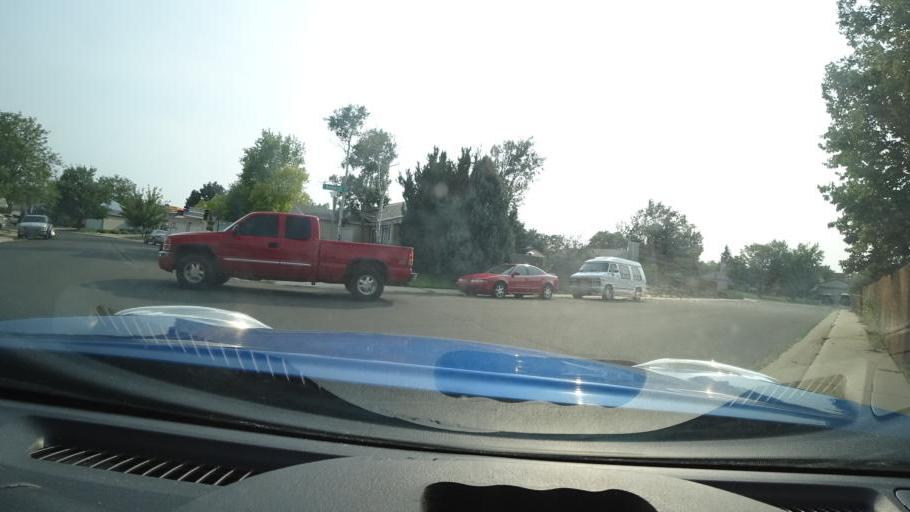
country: US
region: Colorado
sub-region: Adams County
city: Aurora
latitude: 39.6653
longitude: -104.7820
